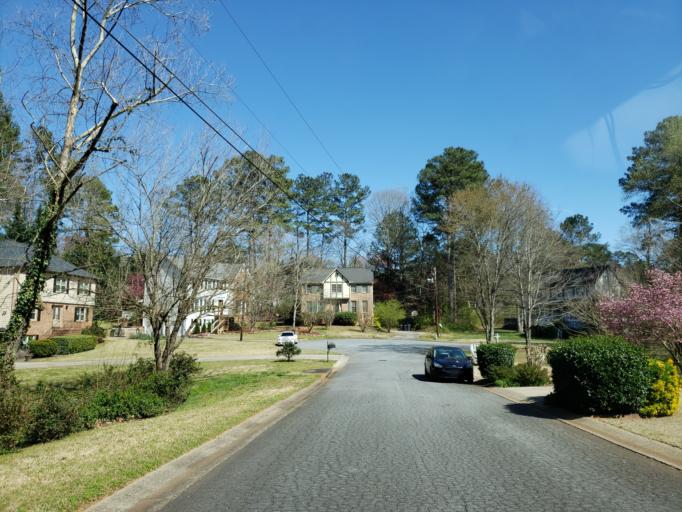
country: US
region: Georgia
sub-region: Cobb County
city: Marietta
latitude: 34.0172
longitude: -84.5132
